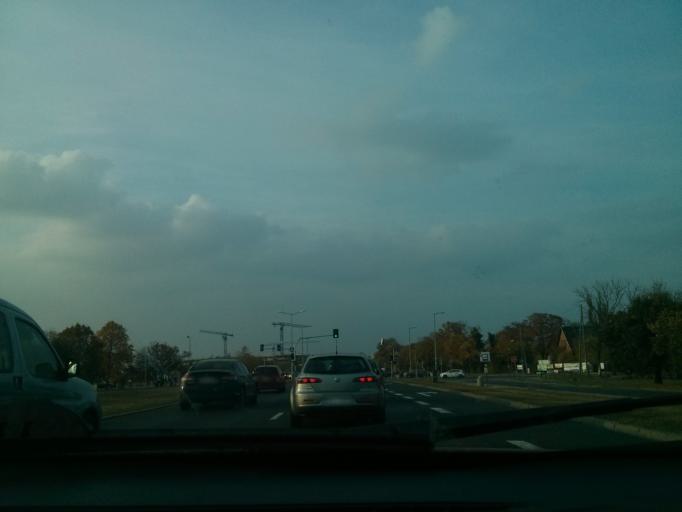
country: PL
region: Masovian Voivodeship
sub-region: Warszawa
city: Wilanow
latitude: 52.1587
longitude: 21.0878
